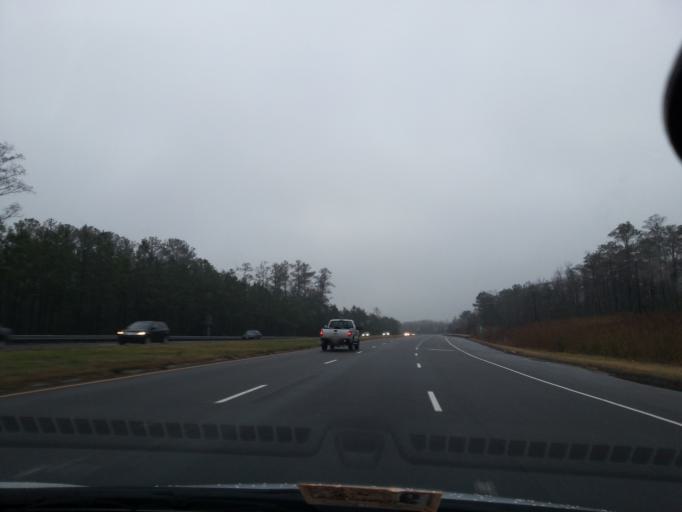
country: US
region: North Carolina
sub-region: Currituck County
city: Moyock
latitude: 36.5736
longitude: -76.1994
